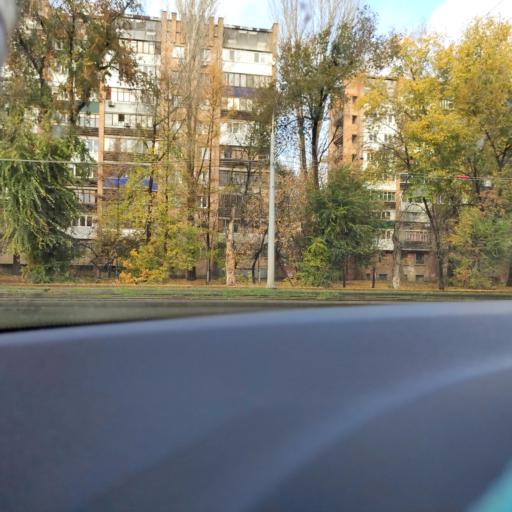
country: RU
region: Samara
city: Smyshlyayevka
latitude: 53.2099
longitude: 50.2833
